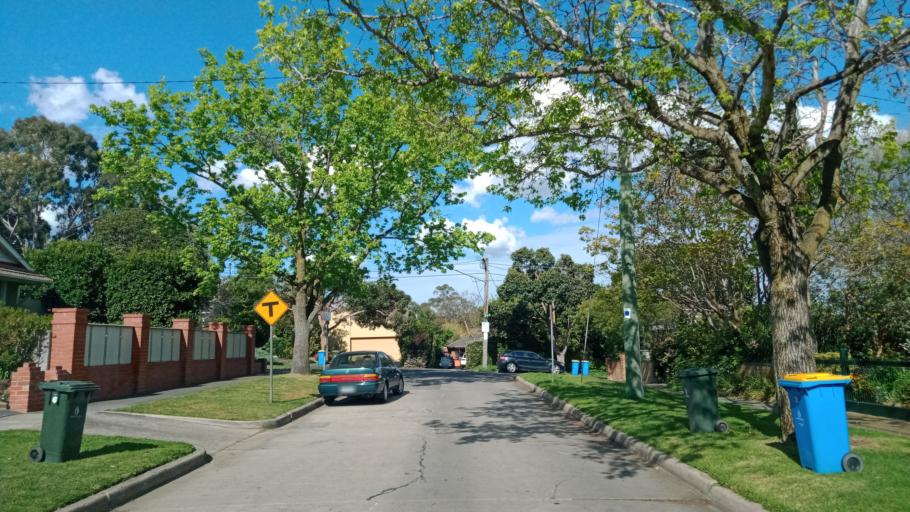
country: AU
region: Victoria
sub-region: Stonnington
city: Glen Iris
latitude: -37.8469
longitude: 145.0562
